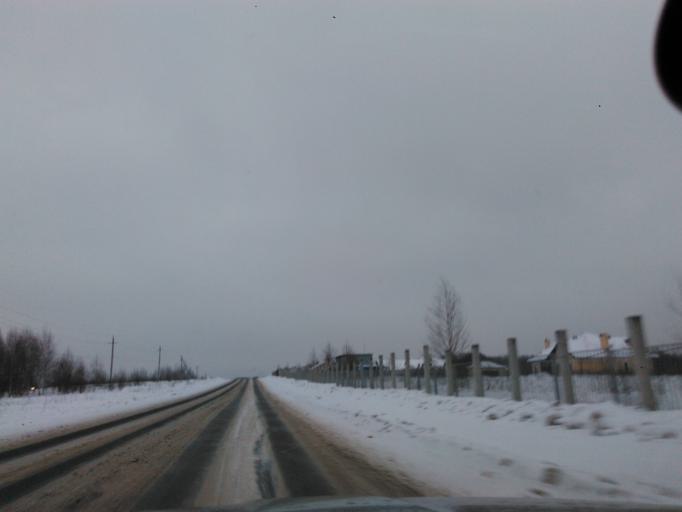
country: RU
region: Moskovskaya
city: Yakhroma
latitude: 56.2700
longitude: 37.4592
